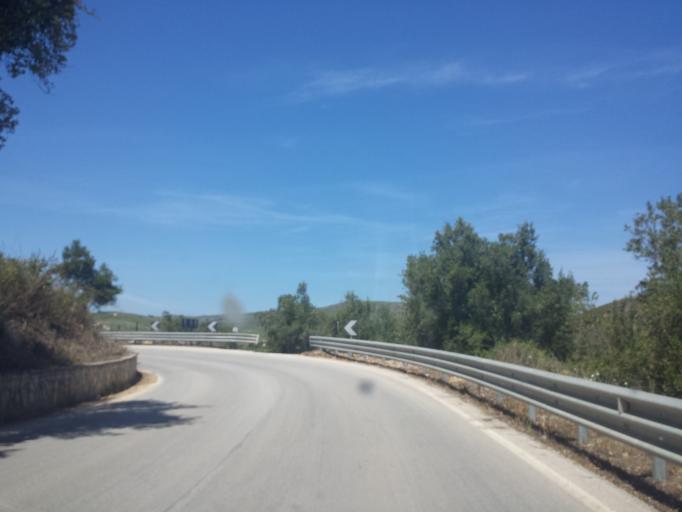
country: IT
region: Sicily
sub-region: Trapani
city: Calatafimi
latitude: 37.9569
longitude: 12.8687
